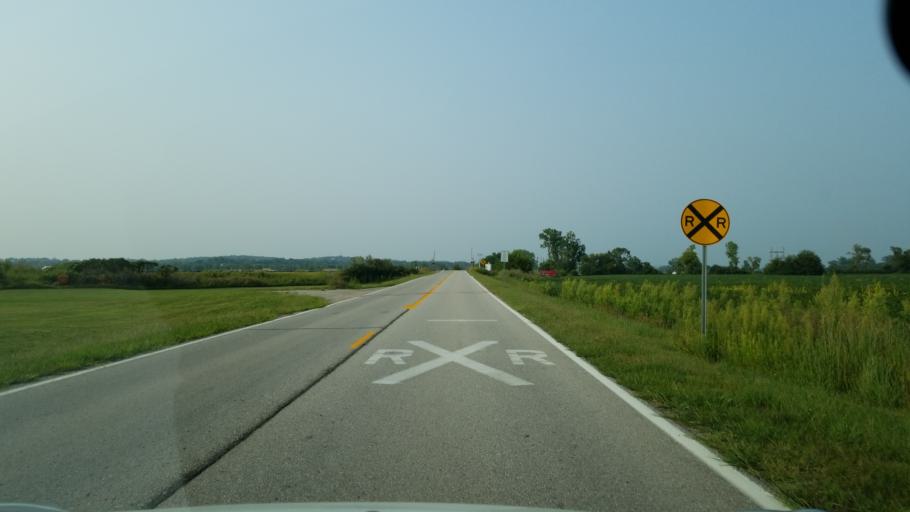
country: US
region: Nebraska
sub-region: Sarpy County
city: Bellevue
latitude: 41.1080
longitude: -95.8899
